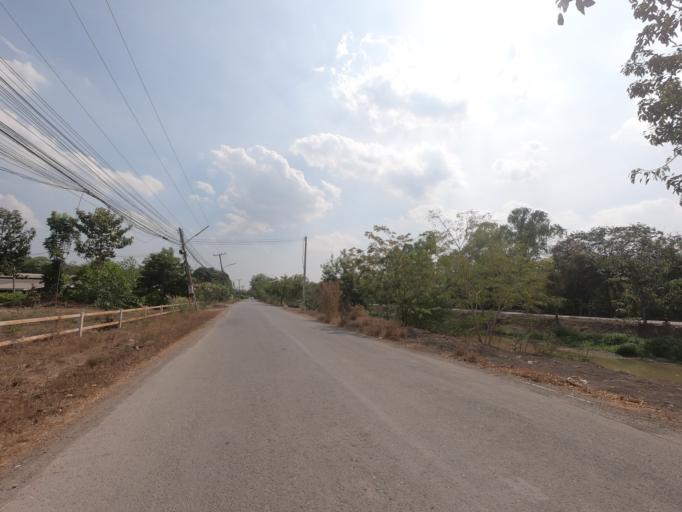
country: TH
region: Pathum Thani
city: Nong Suea
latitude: 14.2012
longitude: 100.8462
